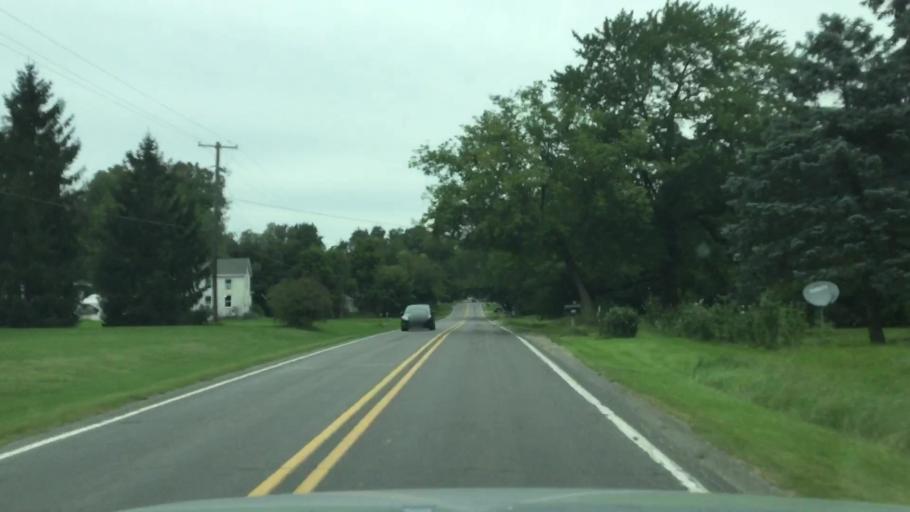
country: US
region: Michigan
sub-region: Washtenaw County
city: Milan
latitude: 42.1630
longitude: -83.6496
